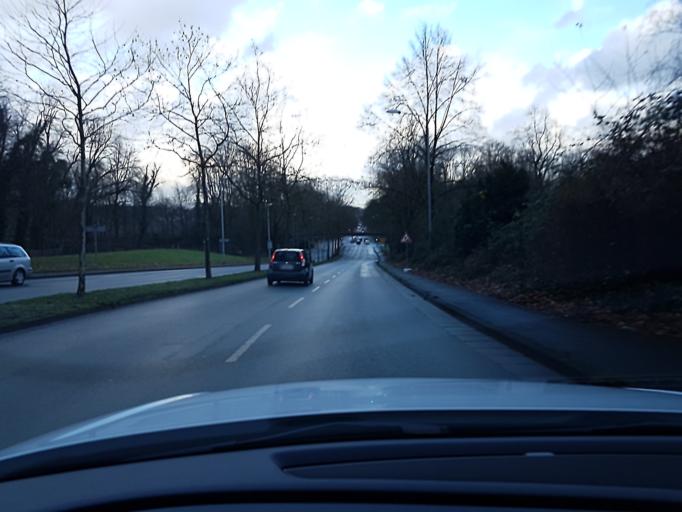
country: DE
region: North Rhine-Westphalia
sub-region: Regierungsbezirk Dusseldorf
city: Muelheim (Ruhr)
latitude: 51.4033
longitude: 6.8804
